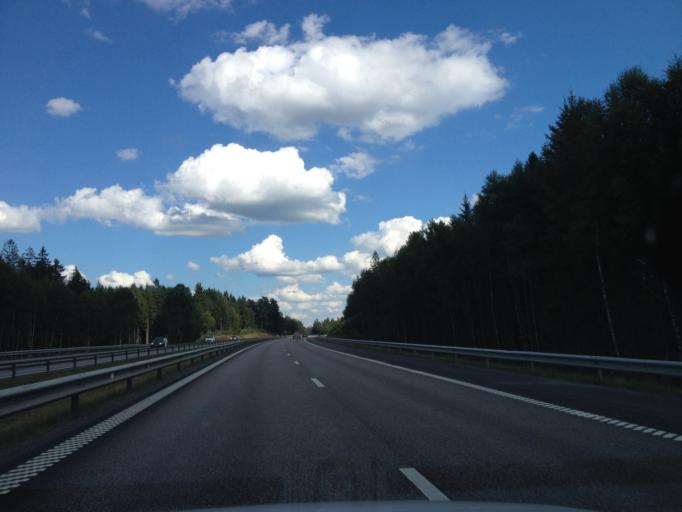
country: SE
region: Vaestra Goetaland
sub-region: Harryda Kommun
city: Landvetter
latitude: 57.7420
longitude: 12.1973
